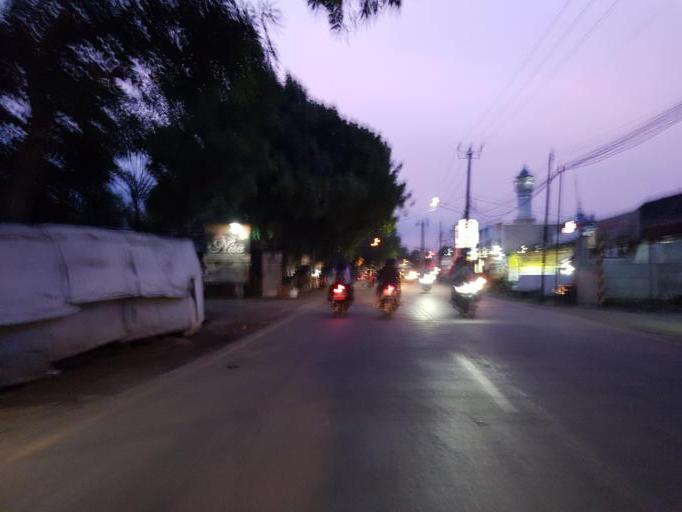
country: ID
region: West Java
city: Serpong
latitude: -6.3244
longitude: 106.6651
